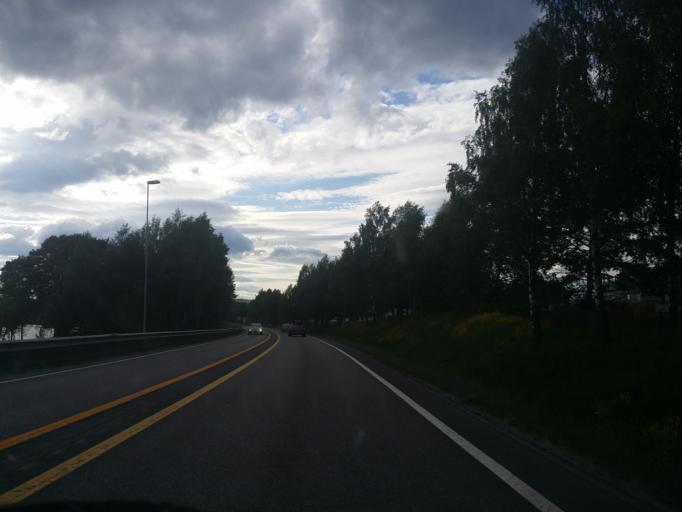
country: NO
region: Hedmark
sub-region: Ringsaker
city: Brumunddal
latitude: 60.8732
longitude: 10.9443
